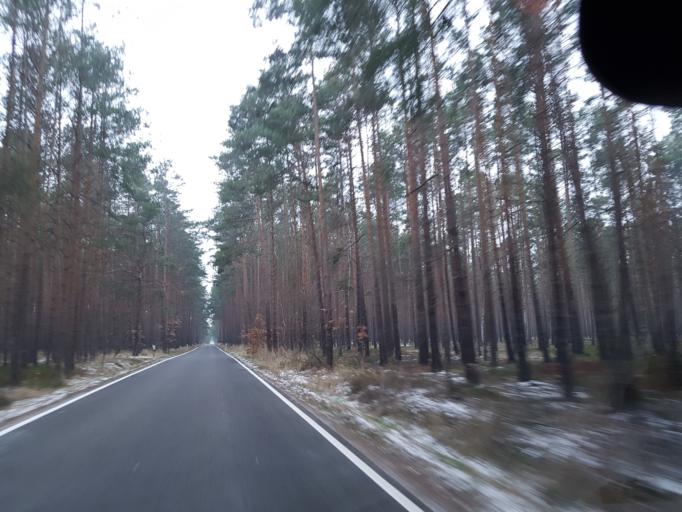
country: DE
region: Brandenburg
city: Ruckersdorf
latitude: 51.5907
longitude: 13.5956
